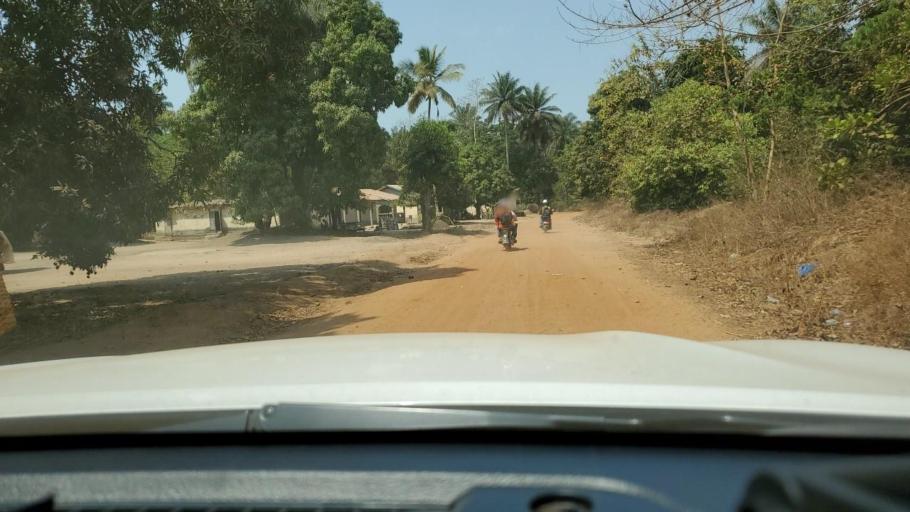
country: GN
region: Boke
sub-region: Boffa
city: Boffa
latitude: 10.0878
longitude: -13.8634
